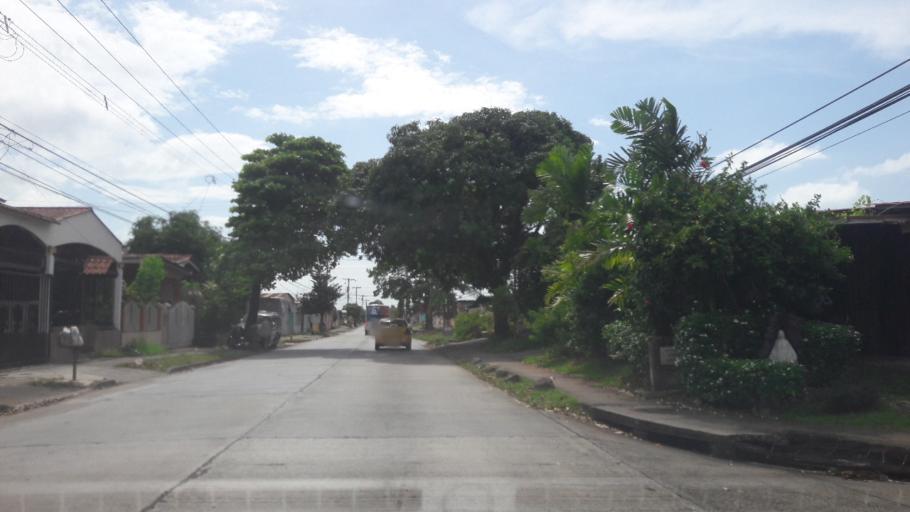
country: PA
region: Panama
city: Tocumen
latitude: 9.0558
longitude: -79.4175
